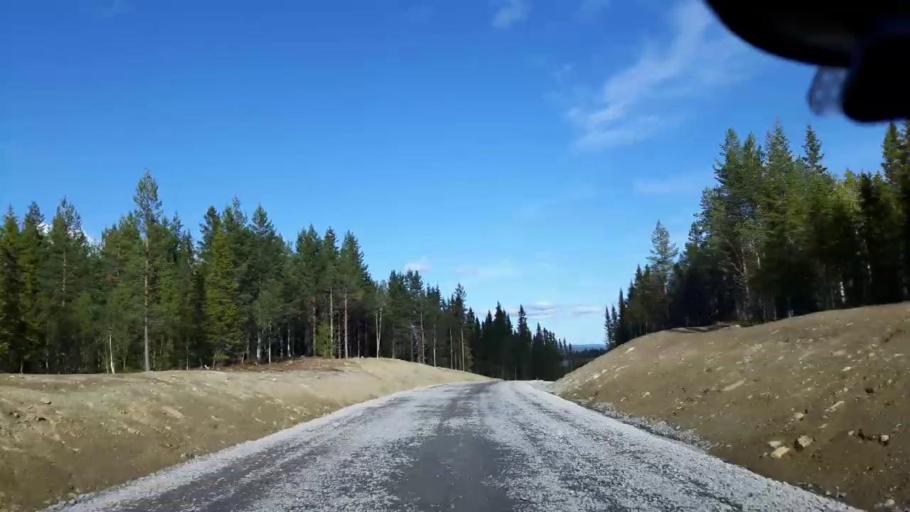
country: SE
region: Jaemtland
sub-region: Ragunda Kommun
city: Hammarstrand
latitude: 63.4242
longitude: 16.1238
